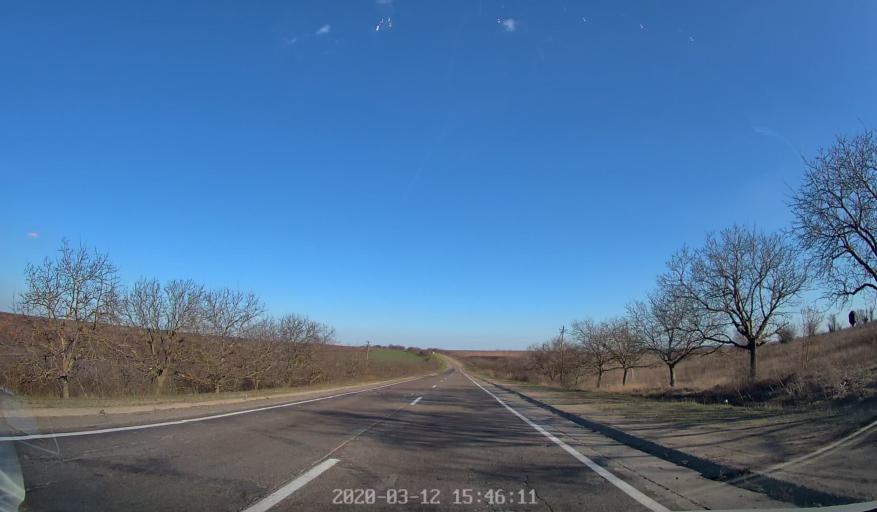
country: MD
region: Chisinau
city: Stauceni
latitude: 47.1011
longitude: 28.8883
